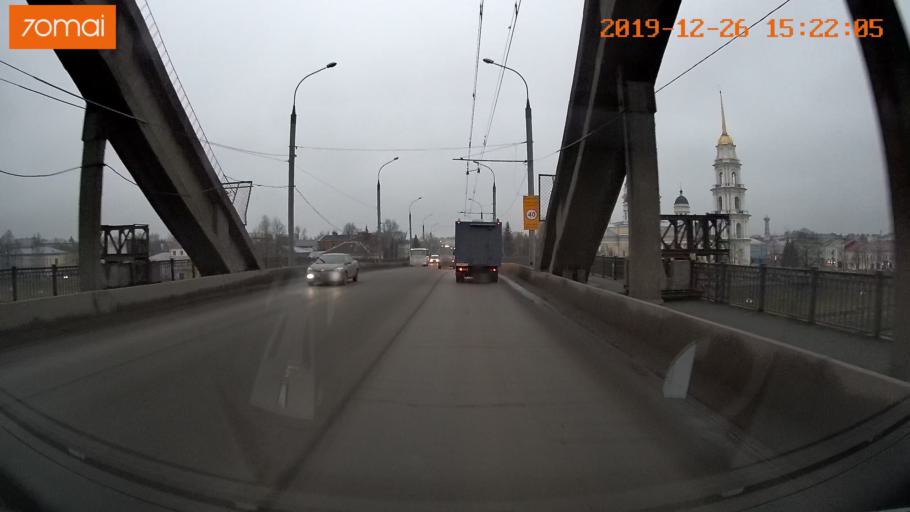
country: RU
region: Jaroslavl
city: Rybinsk
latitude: 58.0496
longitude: 38.8611
